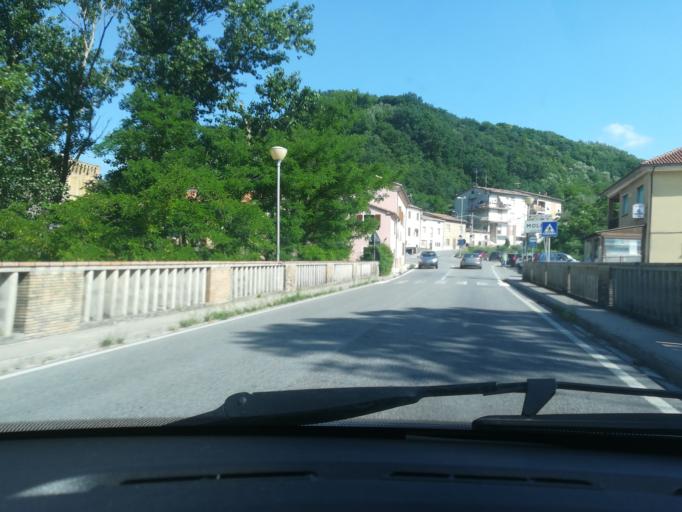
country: IT
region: The Marches
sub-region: Provincia di Macerata
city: Passo di Treia
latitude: 43.2830
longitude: 13.3337
